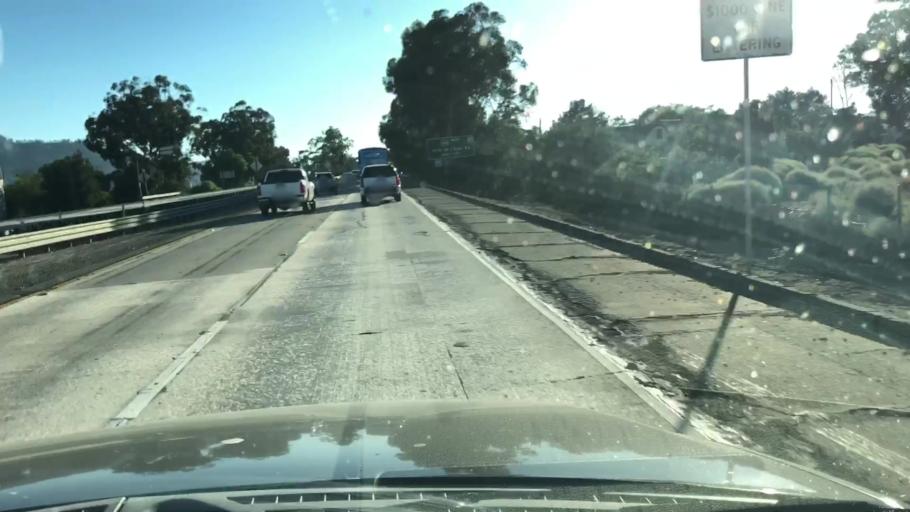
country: US
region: California
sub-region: Ventura County
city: Santa Paula
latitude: 34.3568
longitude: -119.0461
